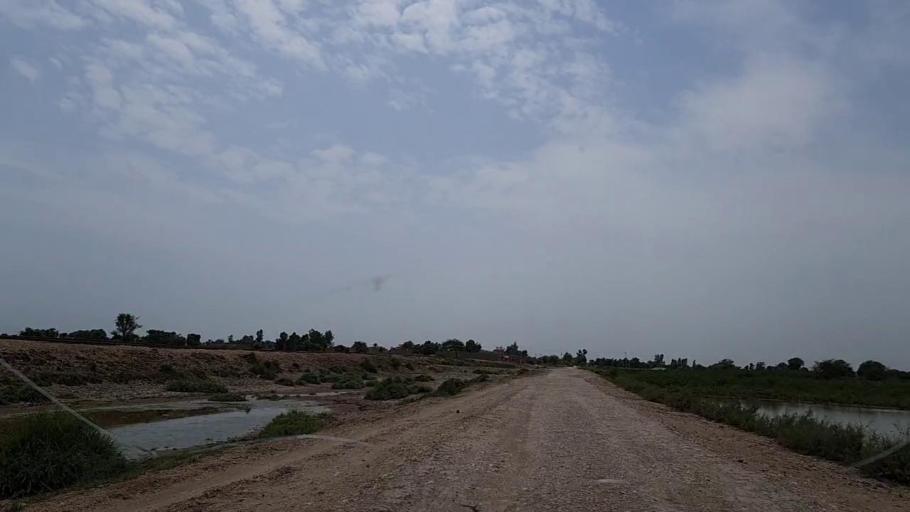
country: PK
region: Sindh
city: Tharu Shah
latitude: 26.9283
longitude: 68.0875
